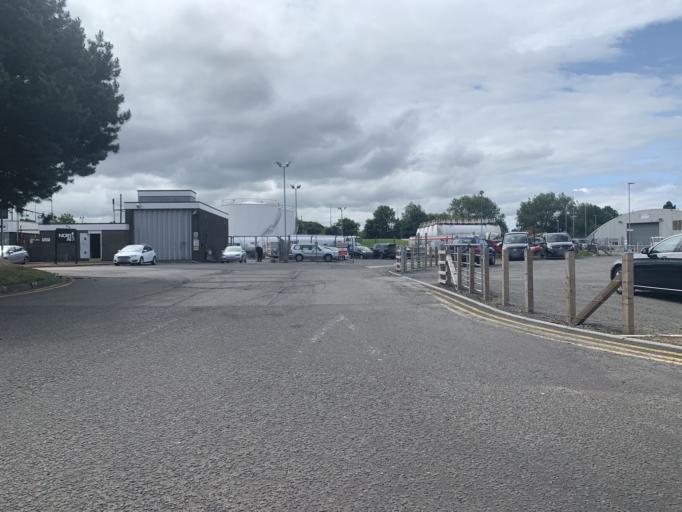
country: GB
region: Scotland
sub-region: Renfrewshire
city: Inchinnan
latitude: 55.8630
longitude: -4.4381
